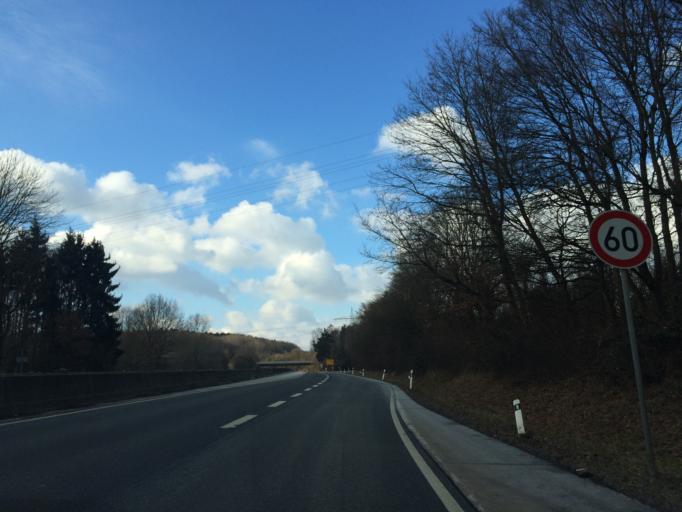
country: DE
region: Hesse
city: Kelkheim (Taunus)
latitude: 50.1502
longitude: 8.4651
